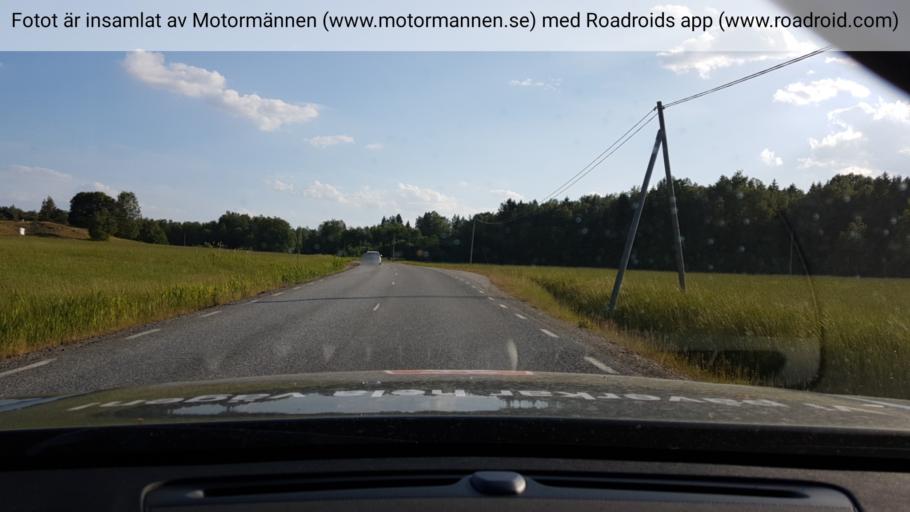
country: SE
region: Stockholm
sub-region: Haninge Kommun
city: Jordbro
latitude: 59.0008
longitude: 18.1102
